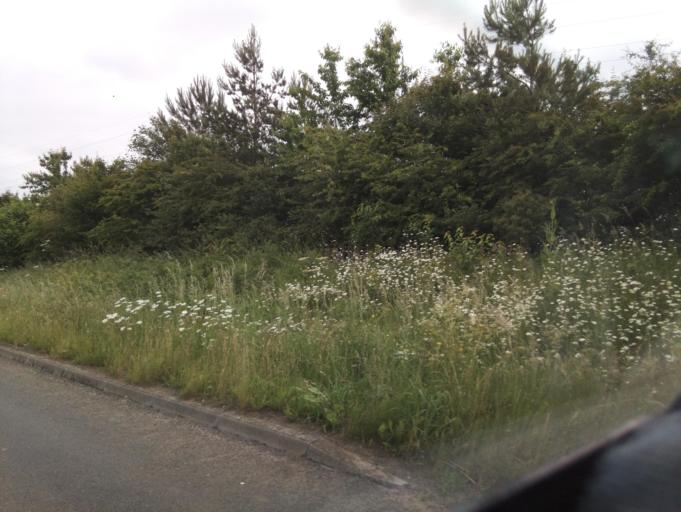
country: GB
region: England
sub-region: District of Rutland
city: Oakham
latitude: 52.6632
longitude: -0.7157
